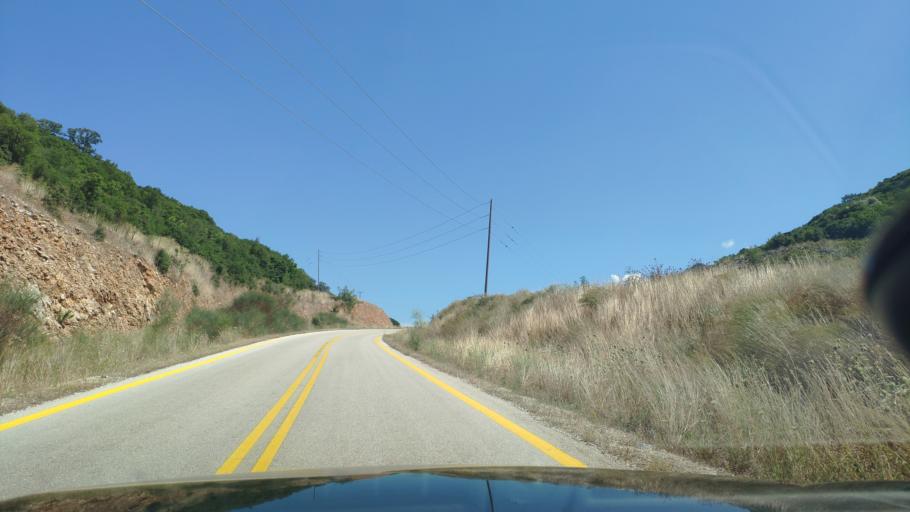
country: GR
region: West Greece
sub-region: Nomos Aitolias kai Akarnanias
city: Amfilochia
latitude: 38.8581
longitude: 21.0855
